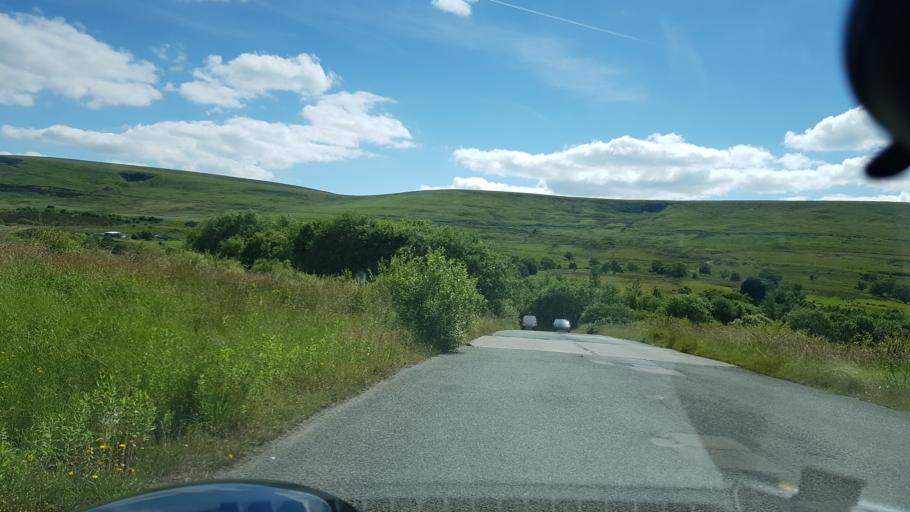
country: GB
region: Wales
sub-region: Torfaen County Borough
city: Blaenavon
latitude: 51.7815
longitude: -3.1097
